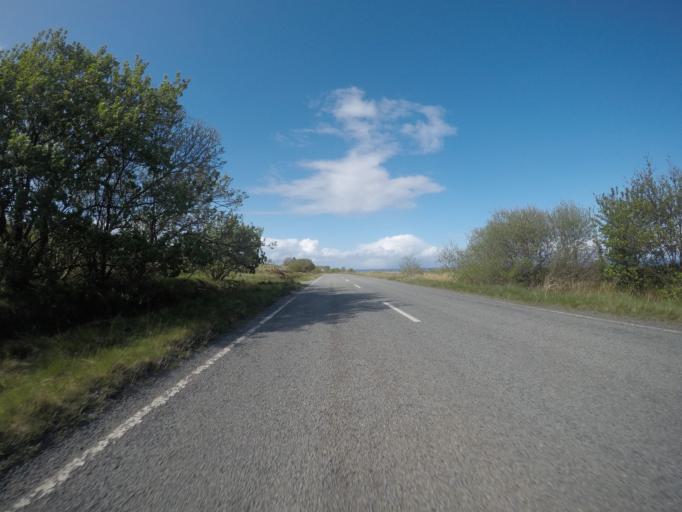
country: GB
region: Scotland
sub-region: Highland
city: Portree
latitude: 57.5891
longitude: -6.1579
